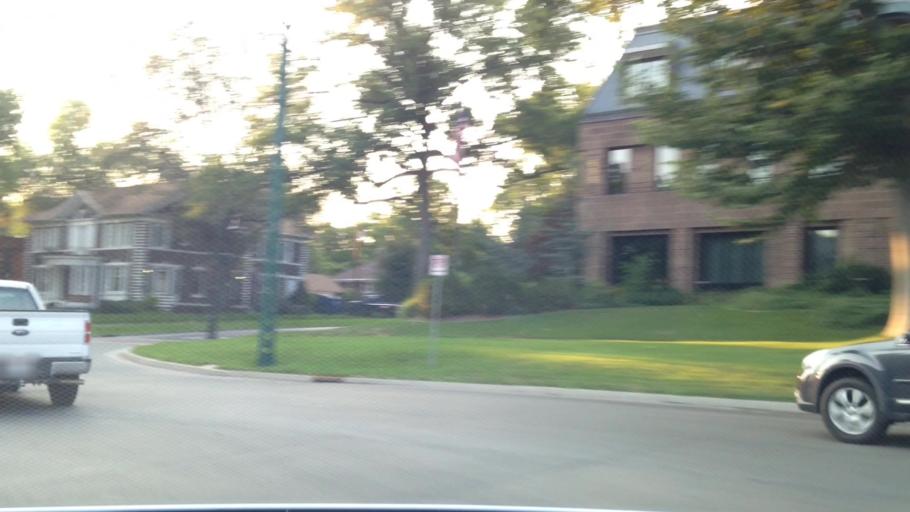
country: US
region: Utah
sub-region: Salt Lake County
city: Salt Lake City
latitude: 40.7693
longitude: -111.8711
